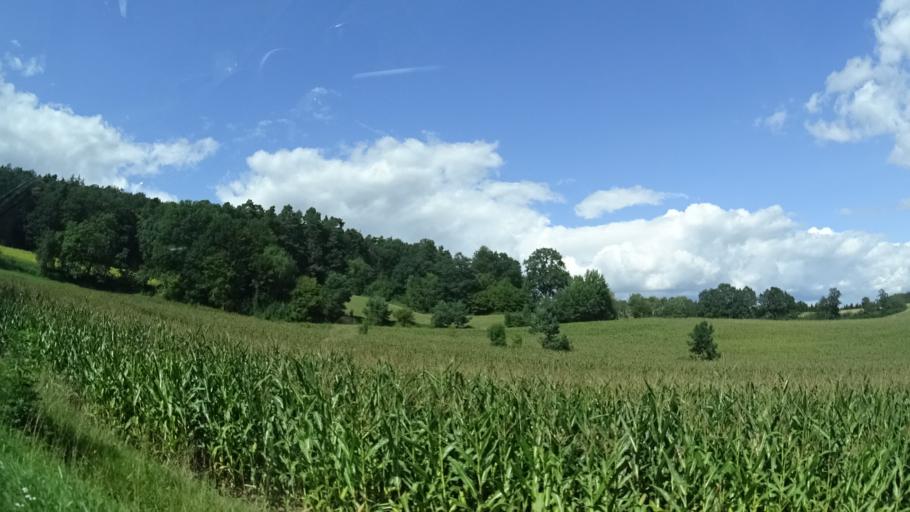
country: DE
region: Bavaria
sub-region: Regierungsbezirk Unterfranken
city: Untermerzbach
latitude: 50.0882
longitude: 10.8412
